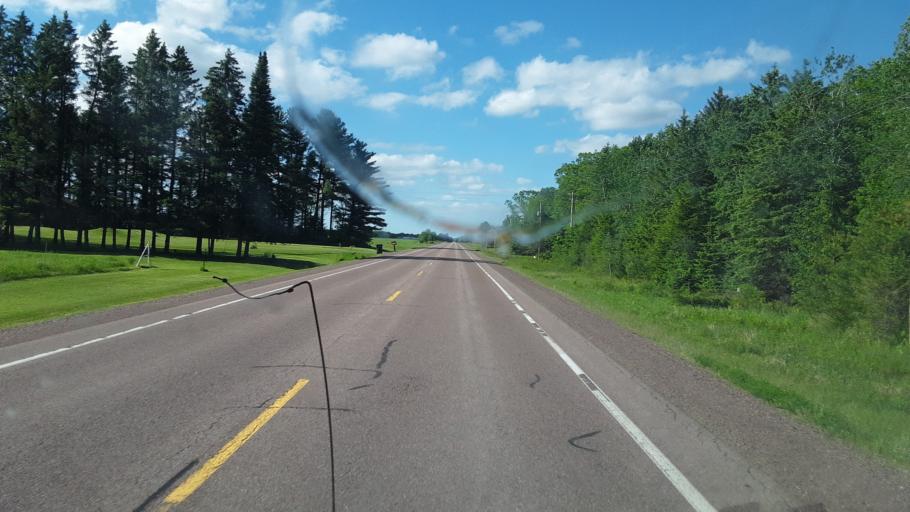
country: US
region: Wisconsin
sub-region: Wood County
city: Marshfield
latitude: 44.4750
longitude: -90.1806
